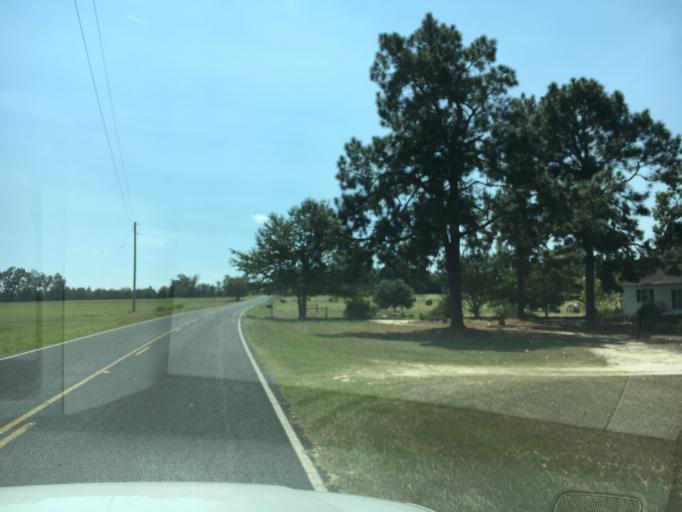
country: US
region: South Carolina
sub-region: Lexington County
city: Batesburg
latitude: 33.8097
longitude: -81.6481
